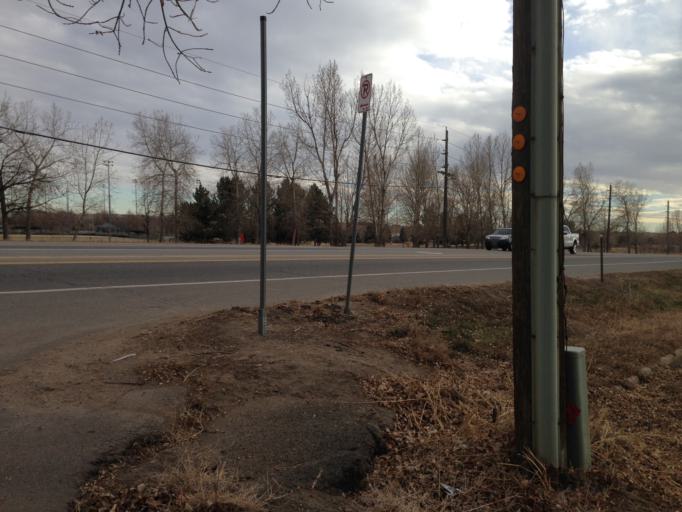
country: US
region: Colorado
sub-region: Boulder County
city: Louisville
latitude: 39.9833
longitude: -105.1281
